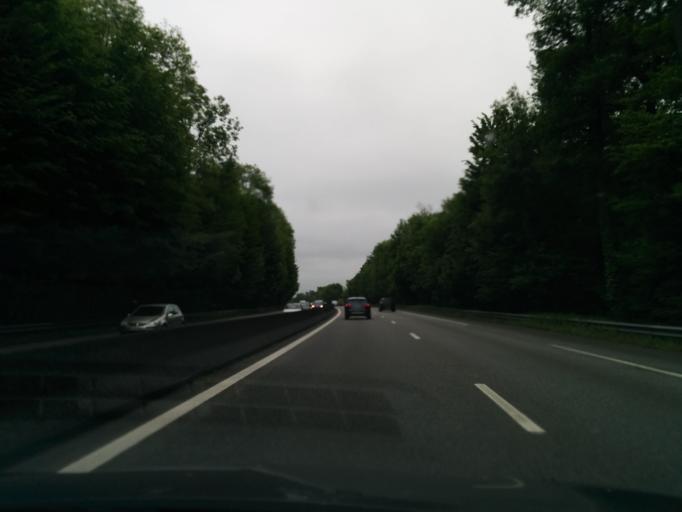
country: FR
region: Ile-de-France
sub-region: Departement des Yvelines
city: Saint-Nom-la-Breteche
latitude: 48.8684
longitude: 2.0316
